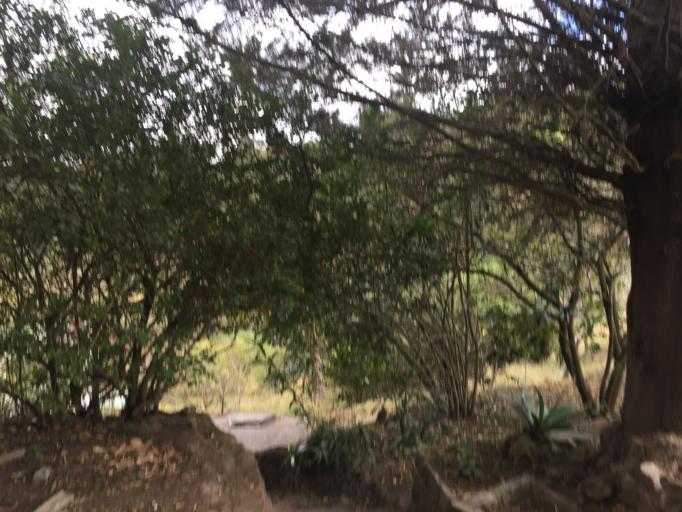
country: EC
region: Pichincha
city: Sangolqui
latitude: -0.2344
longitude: -78.4022
